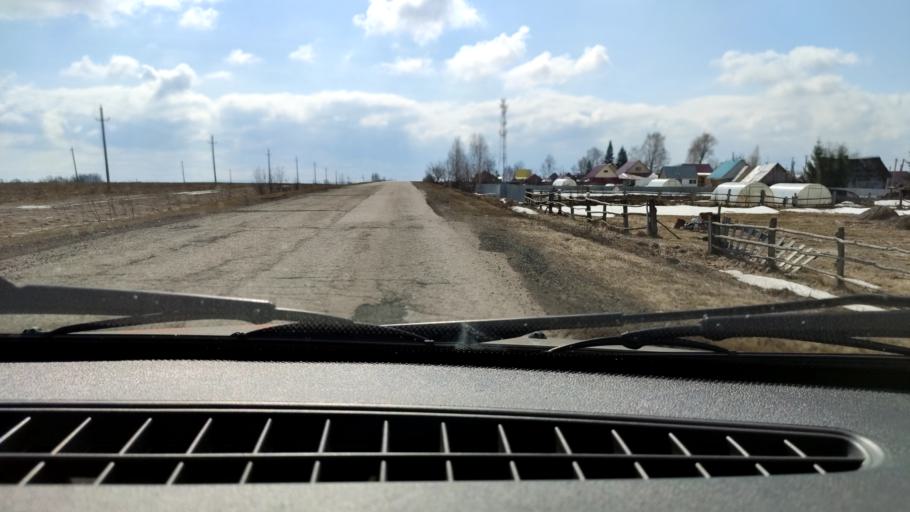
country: RU
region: Bashkortostan
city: Kudeyevskiy
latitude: 54.8484
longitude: 56.7956
